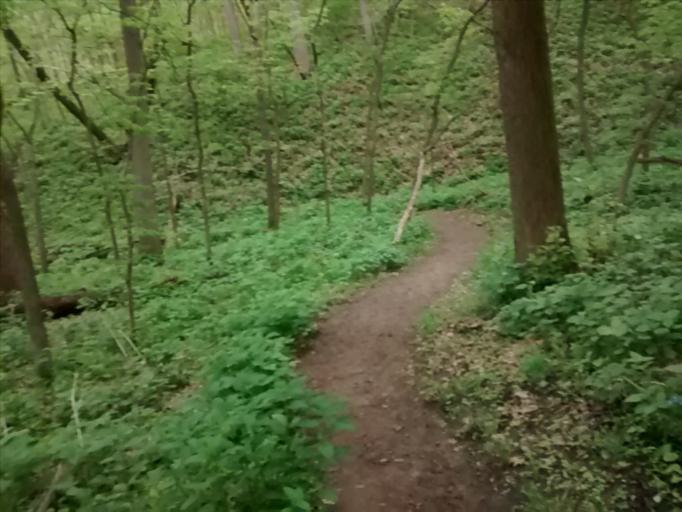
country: US
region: Nebraska
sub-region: Sarpy County
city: Bellevue
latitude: 41.1816
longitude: -95.9060
